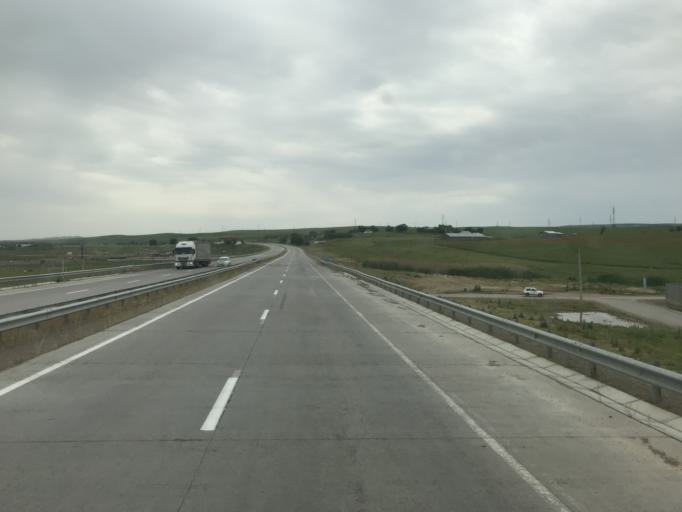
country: KZ
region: Ongtustik Qazaqstan
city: Qazyqurt
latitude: 41.8697
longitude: 69.4204
